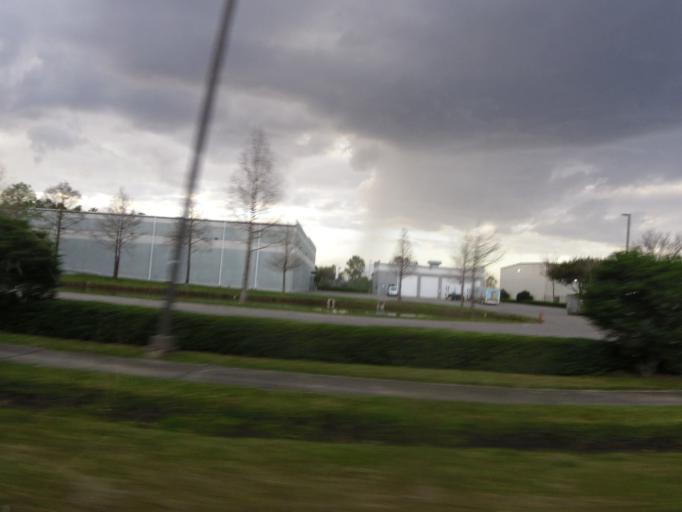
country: US
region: Florida
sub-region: Saint Johns County
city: Fruit Cove
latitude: 30.1865
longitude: -81.5690
